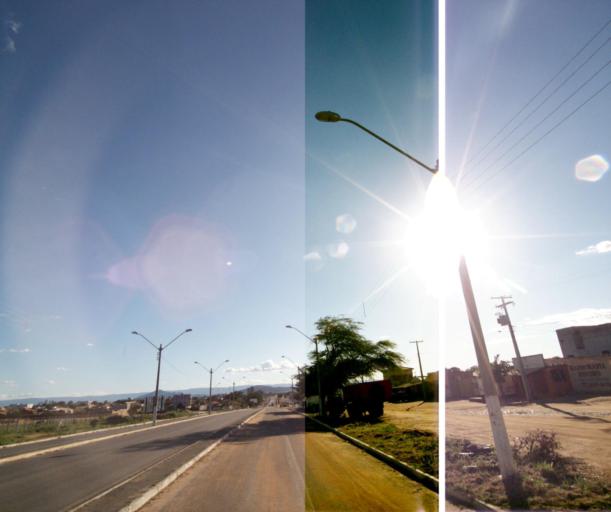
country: BR
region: Bahia
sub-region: Guanambi
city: Guanambi
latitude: -14.2023
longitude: -42.7572
